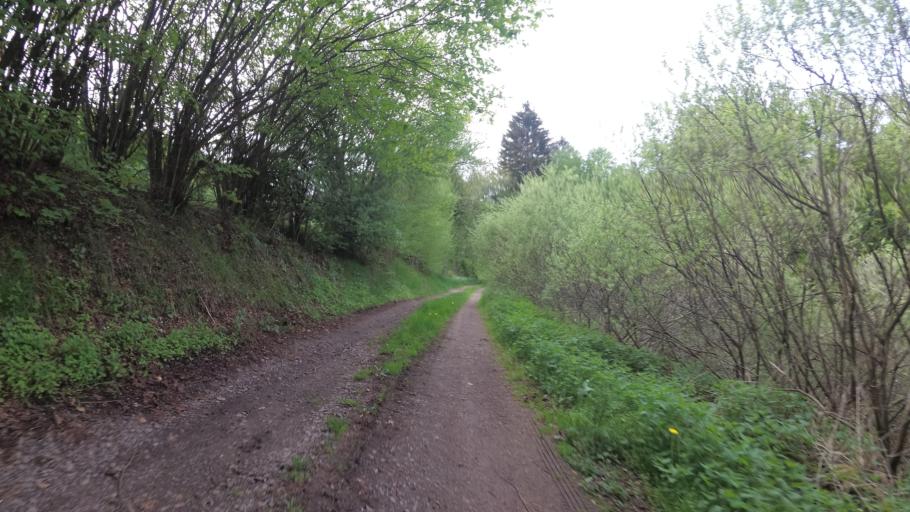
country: DE
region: Rheinland-Pfalz
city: Eckersweiler
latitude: 49.5602
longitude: 7.2822
